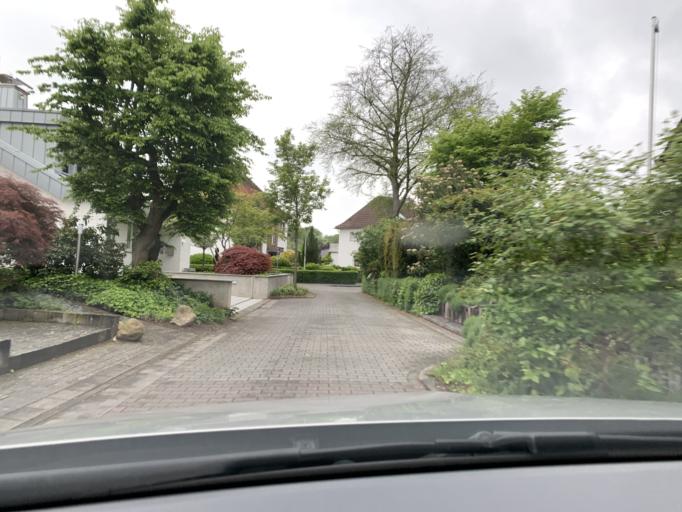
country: DE
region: North Rhine-Westphalia
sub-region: Regierungsbezirk Detmold
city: Rheda-Wiedenbruck
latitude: 51.8326
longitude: 8.3173
